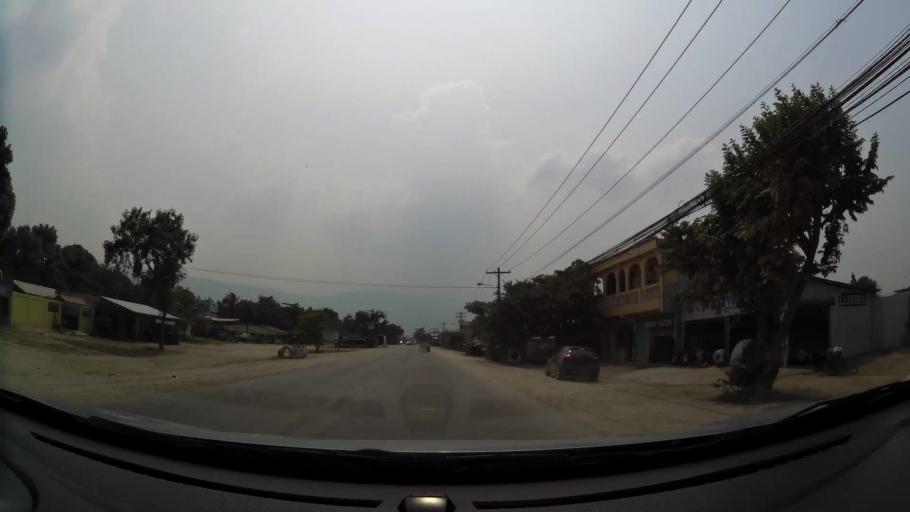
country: HN
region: Cortes
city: San Pedro Sula
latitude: 15.4712
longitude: -87.9966
